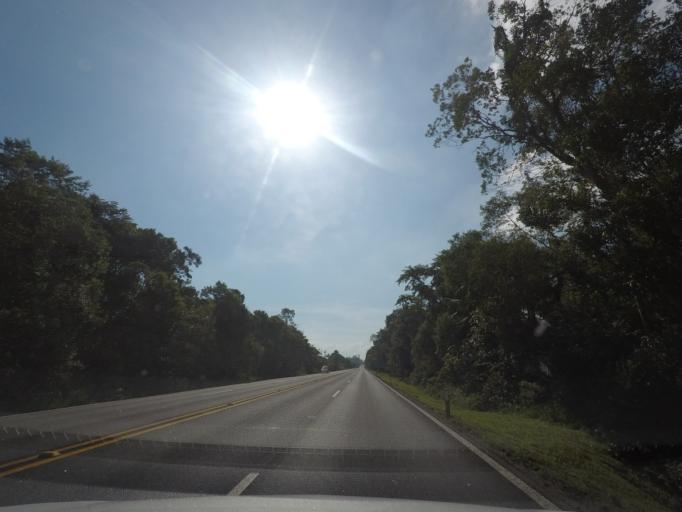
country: BR
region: Parana
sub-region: Pontal Do Parana
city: Pontal do Parana
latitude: -25.6186
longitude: -48.6010
